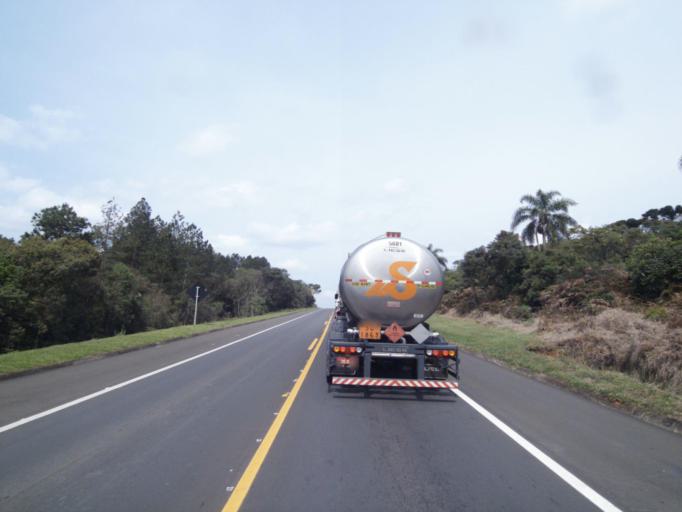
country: BR
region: Parana
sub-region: Irati
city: Irati
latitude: -25.4665
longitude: -50.4122
